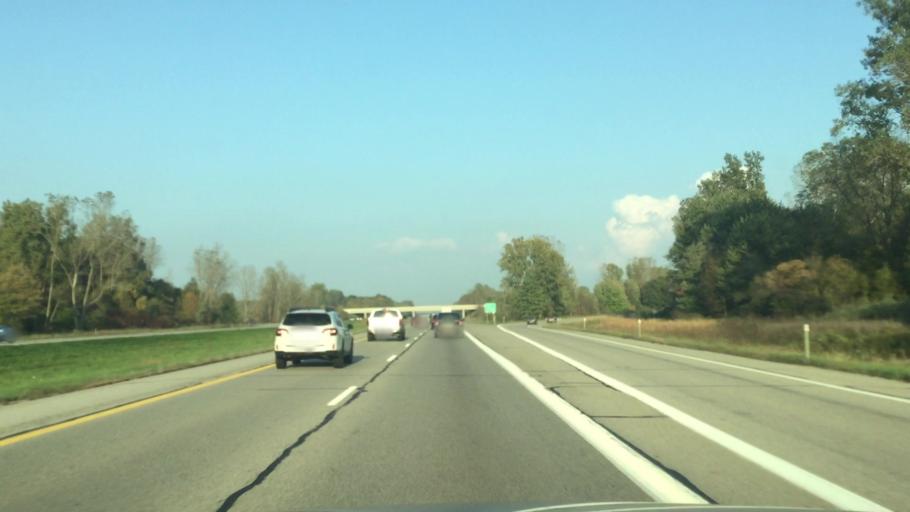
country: US
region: Michigan
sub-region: Wayne County
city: Plymouth
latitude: 42.3597
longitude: -83.5747
